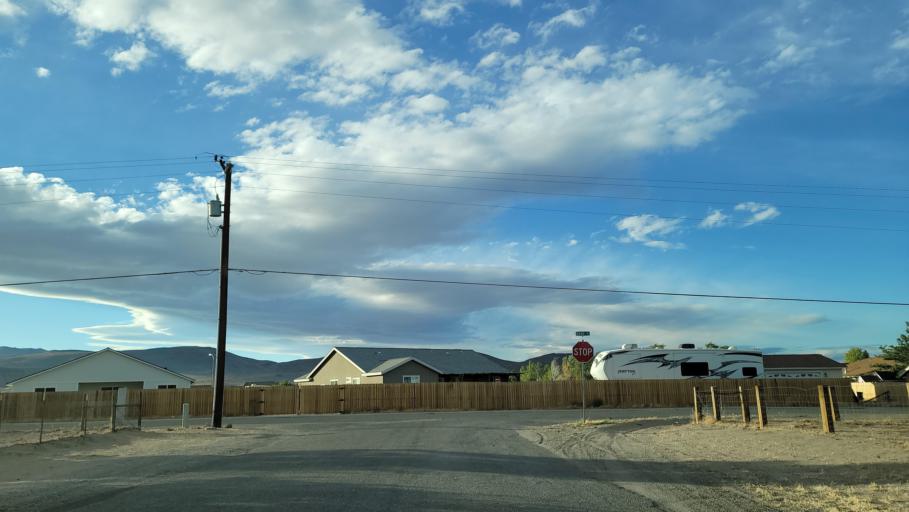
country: US
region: Nevada
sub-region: Lyon County
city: Silver Springs
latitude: 39.4004
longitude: -119.2374
